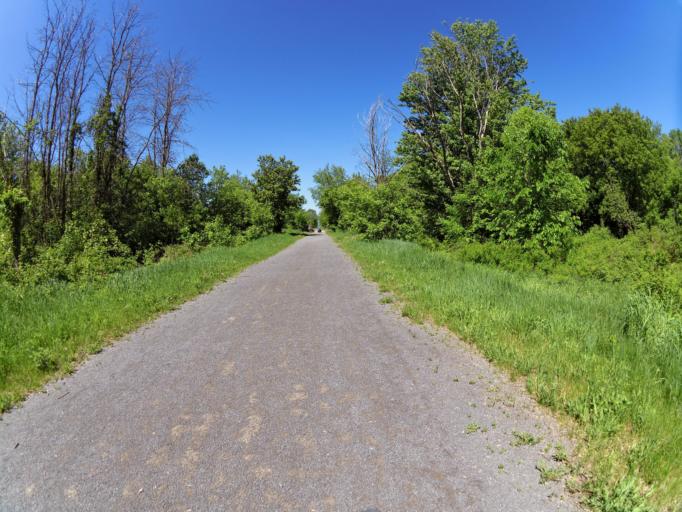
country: CA
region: Ontario
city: Clarence-Rockland
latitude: 45.4147
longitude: -75.4316
